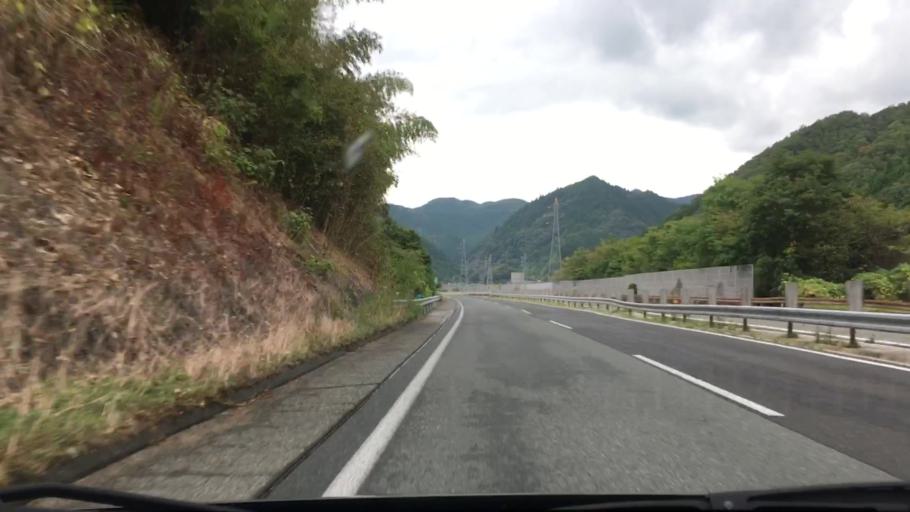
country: JP
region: Okayama
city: Niimi
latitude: 35.0048
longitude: 133.4407
